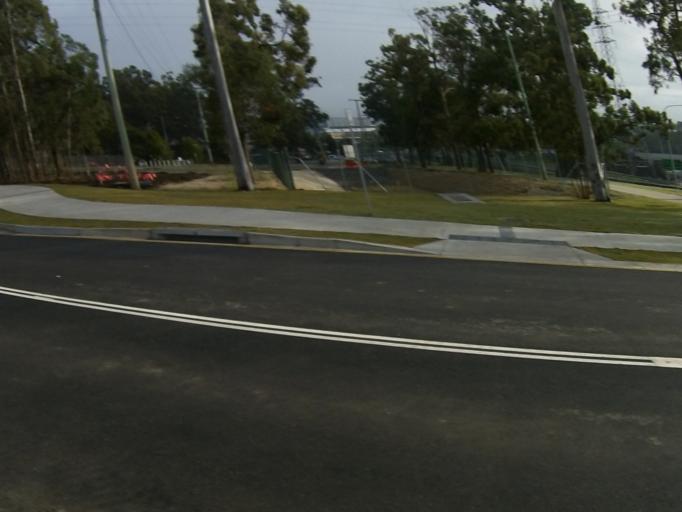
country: AU
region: Queensland
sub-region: Brisbane
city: Upper Mount Gravatt
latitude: -27.5716
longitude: 153.0898
